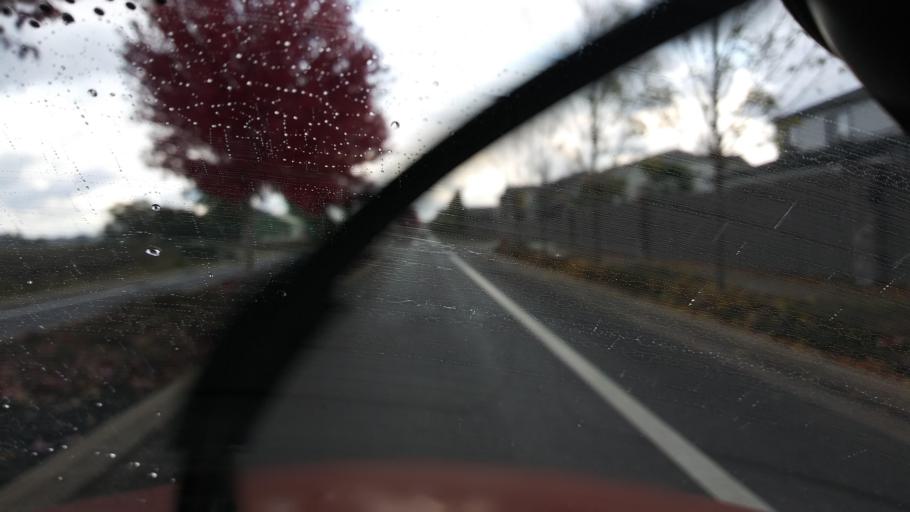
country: US
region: Oregon
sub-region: Washington County
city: Forest Grove
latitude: 45.5391
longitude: -123.1178
